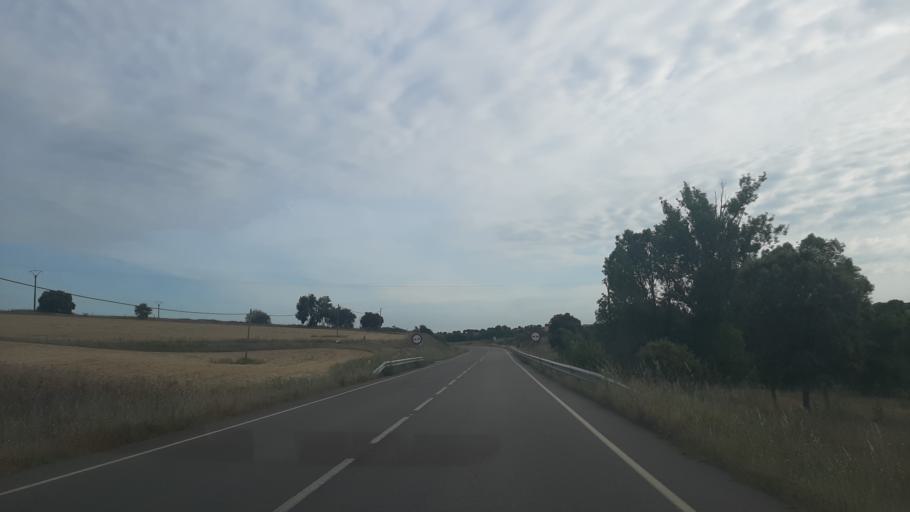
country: ES
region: Castille and Leon
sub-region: Provincia de Salamanca
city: Gallegos de Arganan
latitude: 40.5979
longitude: -6.7040
